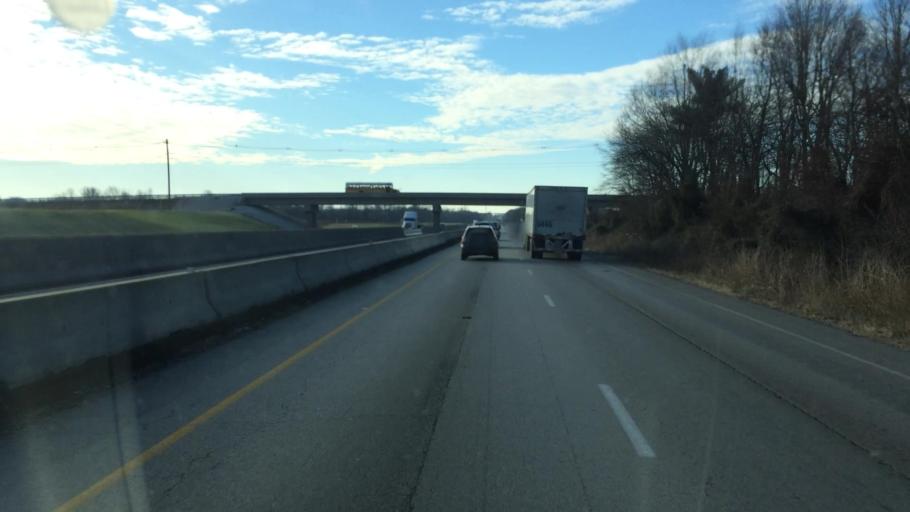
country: US
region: Kentucky
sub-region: Hardin County
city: Elizabethtown
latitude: 37.5752
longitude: -85.8734
